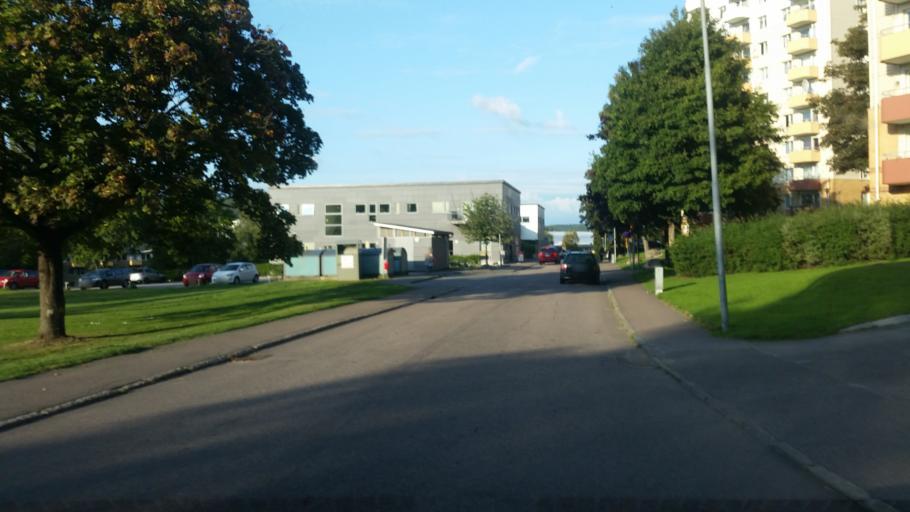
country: SE
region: Vaestra Goetaland
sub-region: Partille Kommun
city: Partille
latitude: 57.7366
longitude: 12.1114
